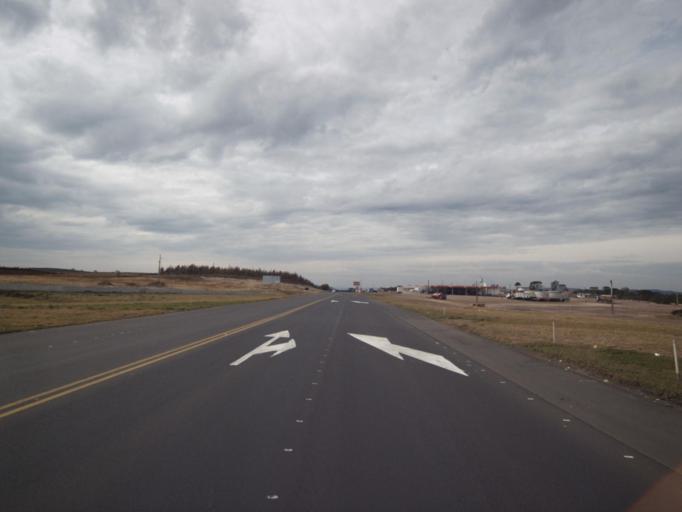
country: BR
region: Santa Catarina
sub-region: Cacador
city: Cacador
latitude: -26.6092
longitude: -51.4788
